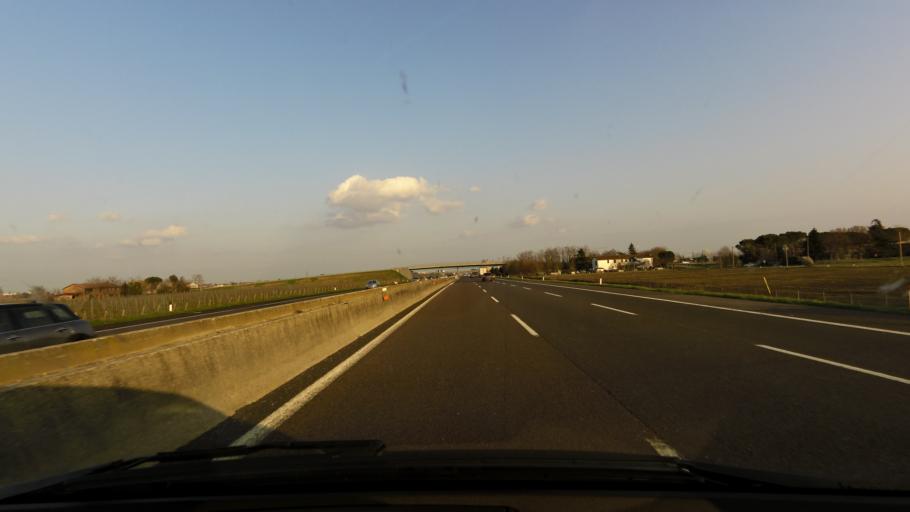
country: IT
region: Emilia-Romagna
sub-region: Provincia di Bologna
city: Imola
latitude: 44.3913
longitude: 11.7122
